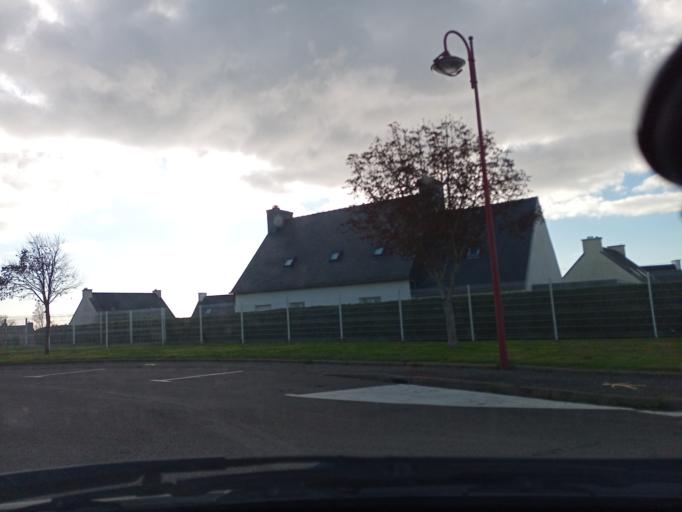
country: FR
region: Brittany
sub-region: Departement du Finistere
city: Plouhinec
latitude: 48.0166
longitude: -4.4913
